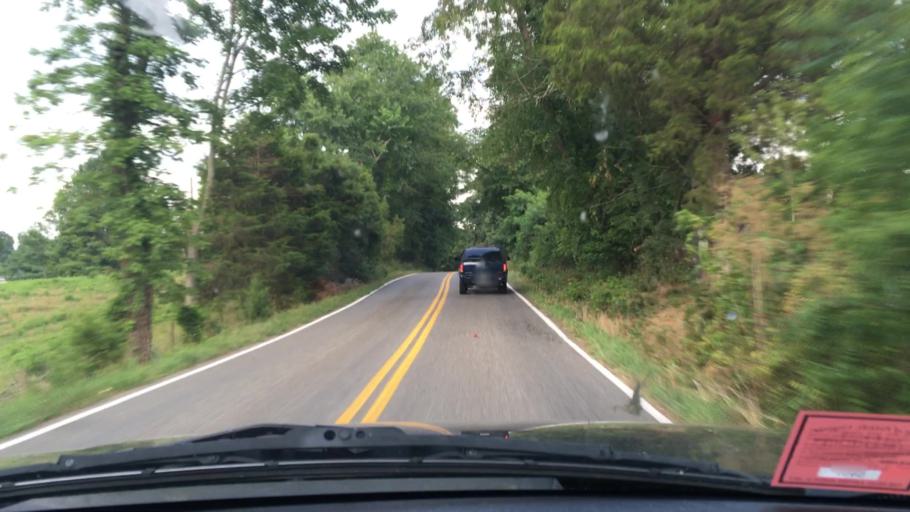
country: US
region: Virginia
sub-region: Pulaski County
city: Dublin
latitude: 37.0534
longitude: -80.6955
